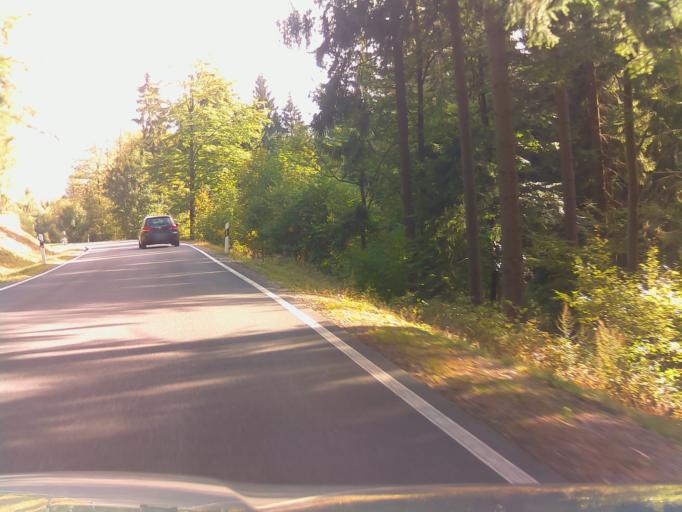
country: DE
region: Thuringia
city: Zella-Mehlis
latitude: 50.6763
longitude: 10.6491
